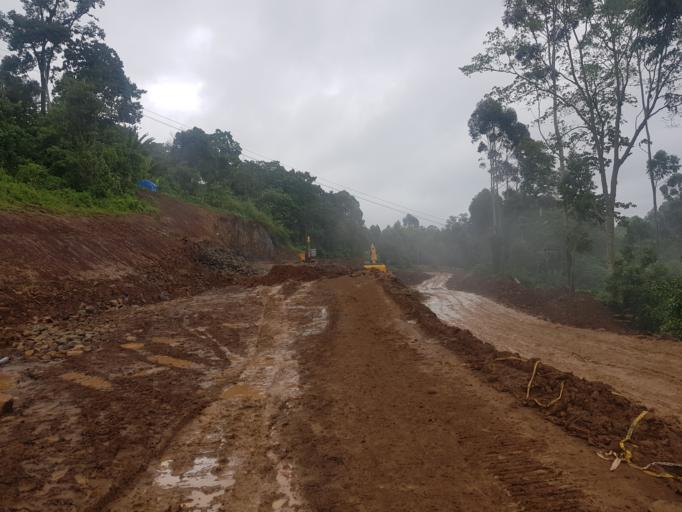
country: ET
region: Oromiya
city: Gore
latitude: 7.7058
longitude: 35.4897
